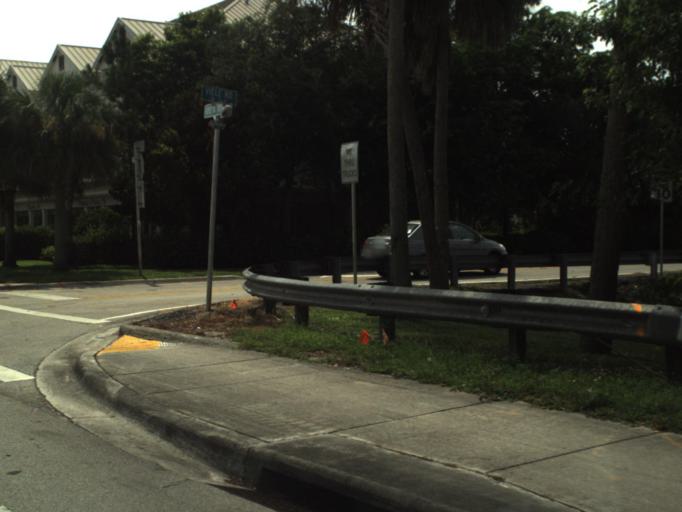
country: US
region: Florida
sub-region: Broward County
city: Davie
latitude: 26.0648
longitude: -80.2403
